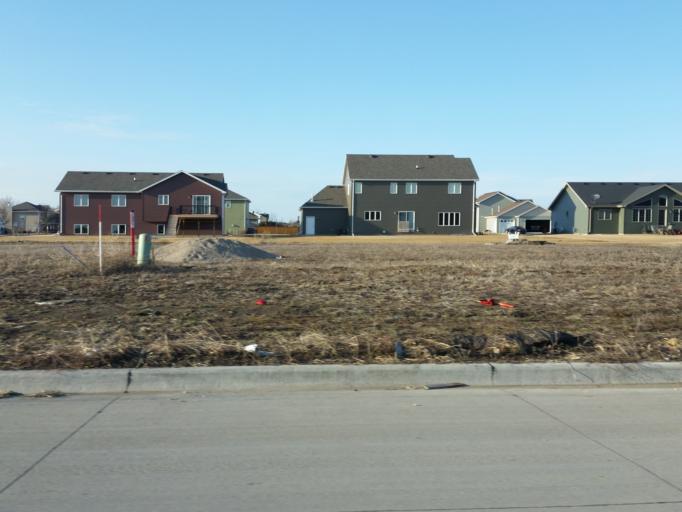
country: US
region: North Dakota
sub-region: Grand Forks County
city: Grand Forks
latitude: 47.8640
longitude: -97.0275
